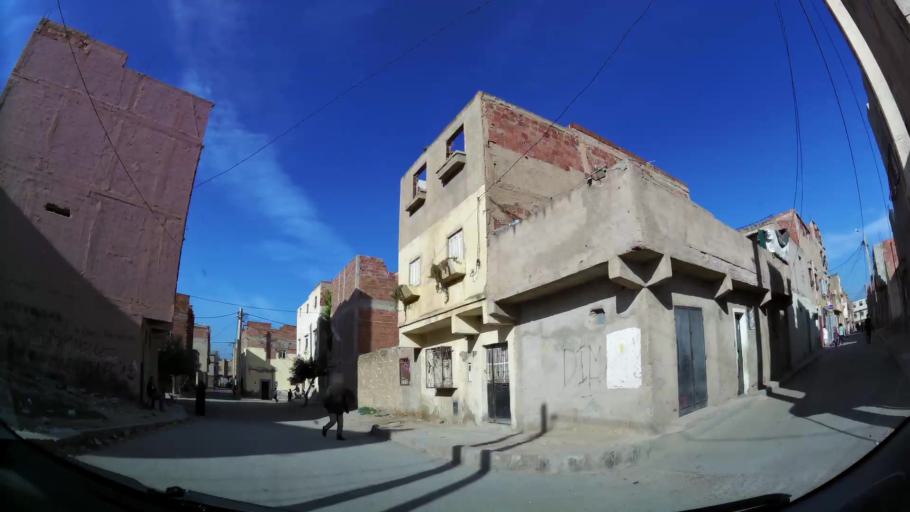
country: MA
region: Oriental
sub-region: Oujda-Angad
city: Oujda
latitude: 34.7141
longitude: -1.8923
